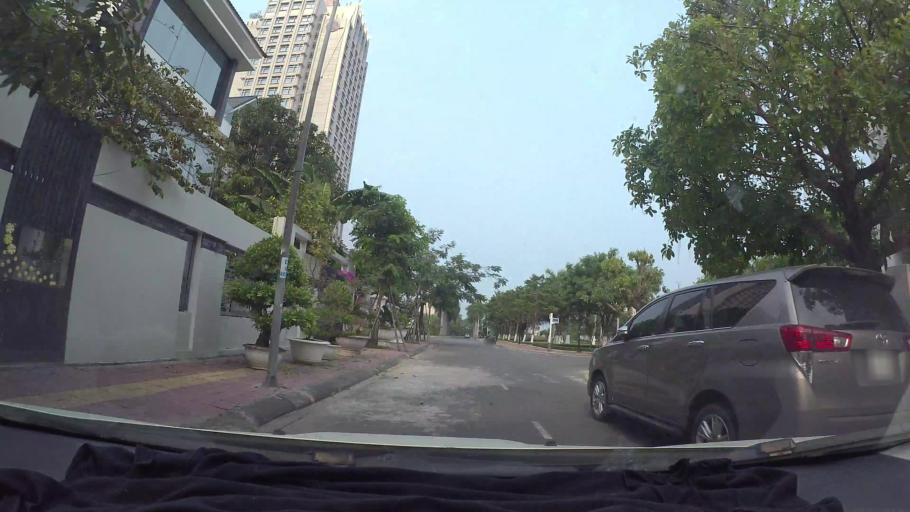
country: VN
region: Da Nang
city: Son Tra
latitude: 16.0473
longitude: 108.2263
